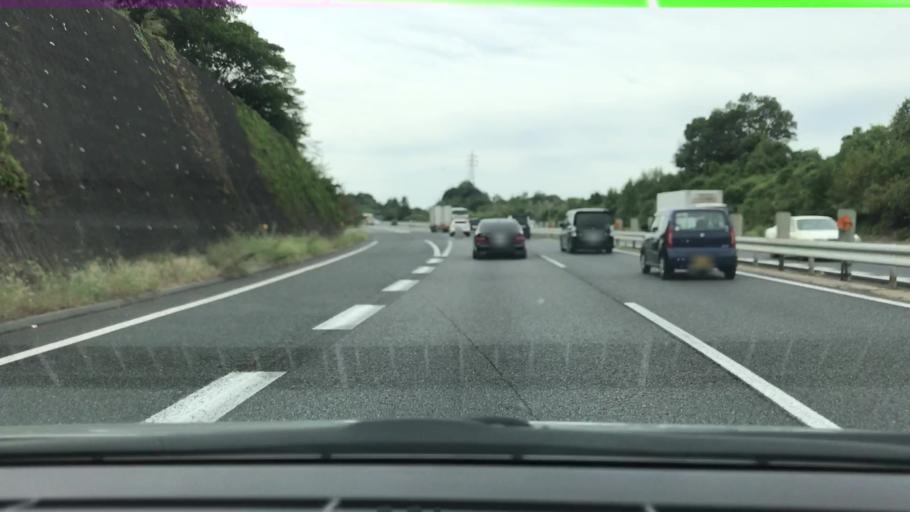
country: JP
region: Hyogo
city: Aioi
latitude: 34.8218
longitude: 134.4614
